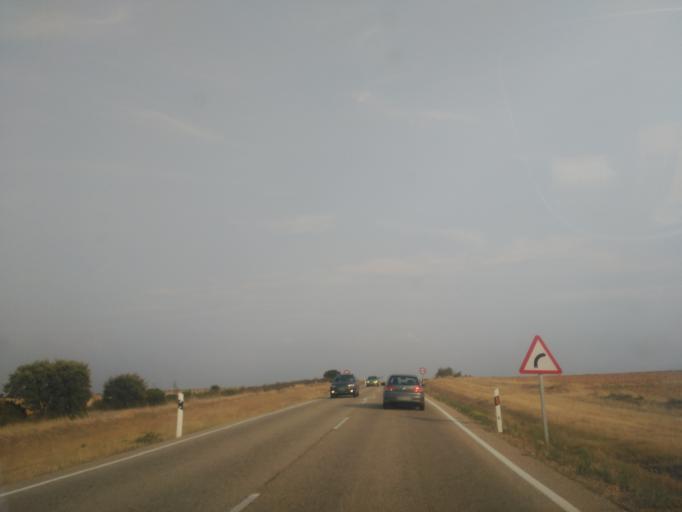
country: ES
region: Castille and Leon
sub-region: Provincia de Zamora
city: Tabara
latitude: 41.8494
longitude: -5.9849
